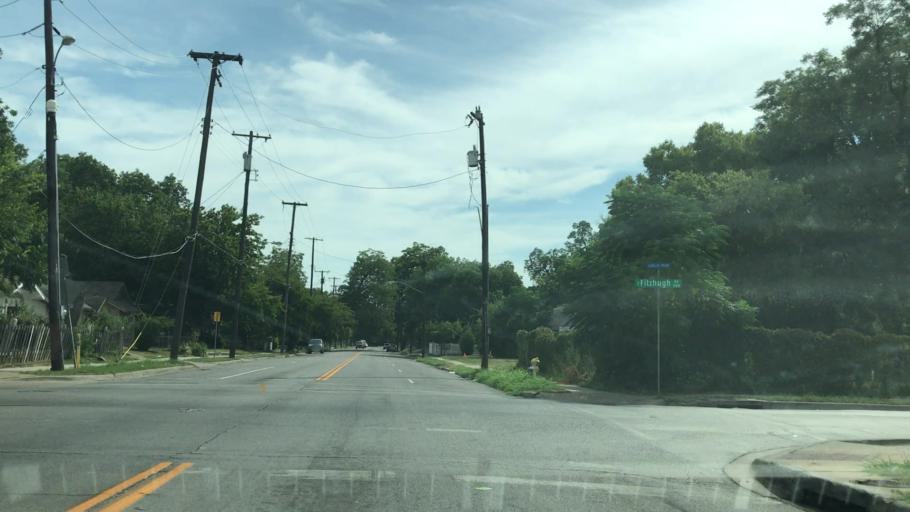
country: US
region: Texas
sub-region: Dallas County
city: Dallas
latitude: 32.7905
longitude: -96.7580
